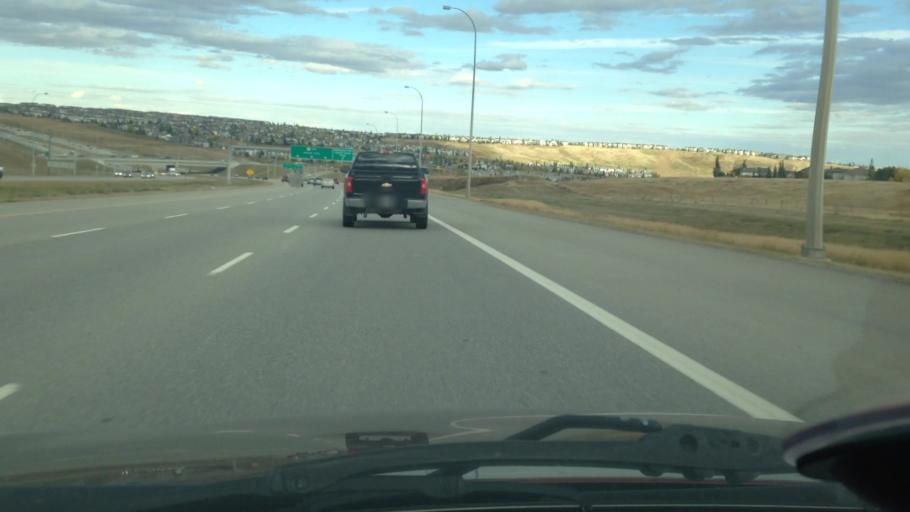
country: CA
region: Alberta
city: Calgary
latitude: 51.1533
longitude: -114.1254
